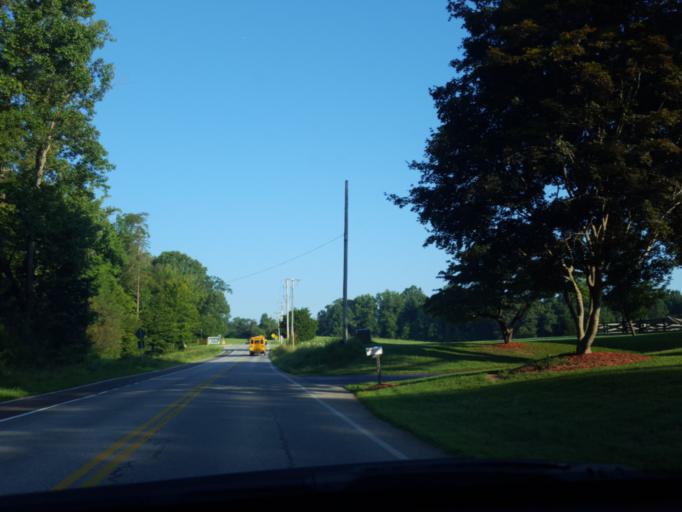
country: US
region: Maryland
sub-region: Calvert County
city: Huntingtown
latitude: 38.6102
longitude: -76.5926
